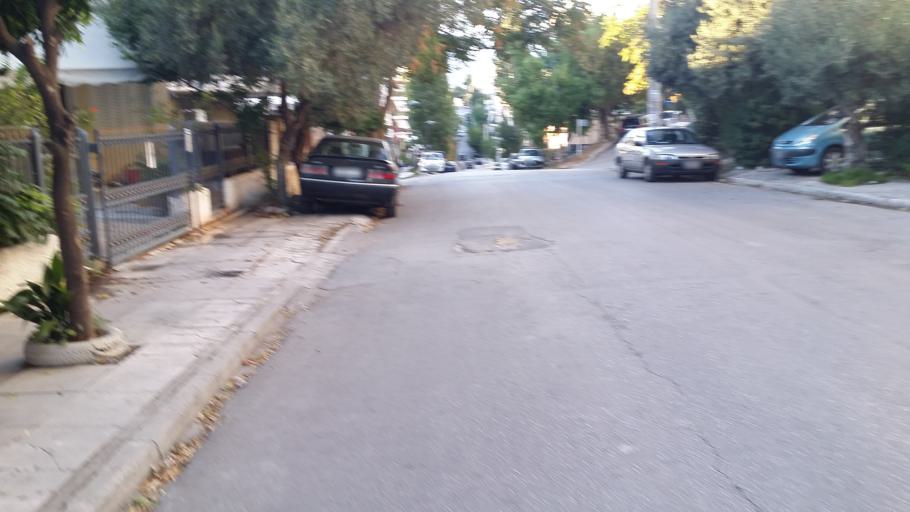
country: GR
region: Attica
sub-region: Nomarchia Athinas
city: Irakleio
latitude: 38.0529
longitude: 23.7592
